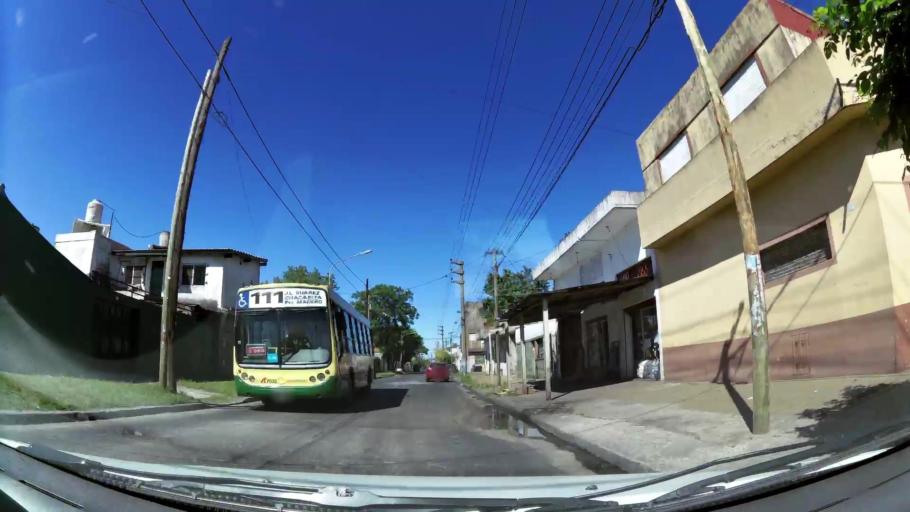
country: AR
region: Buenos Aires
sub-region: Partido de General San Martin
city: General San Martin
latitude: -34.5430
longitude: -58.5331
